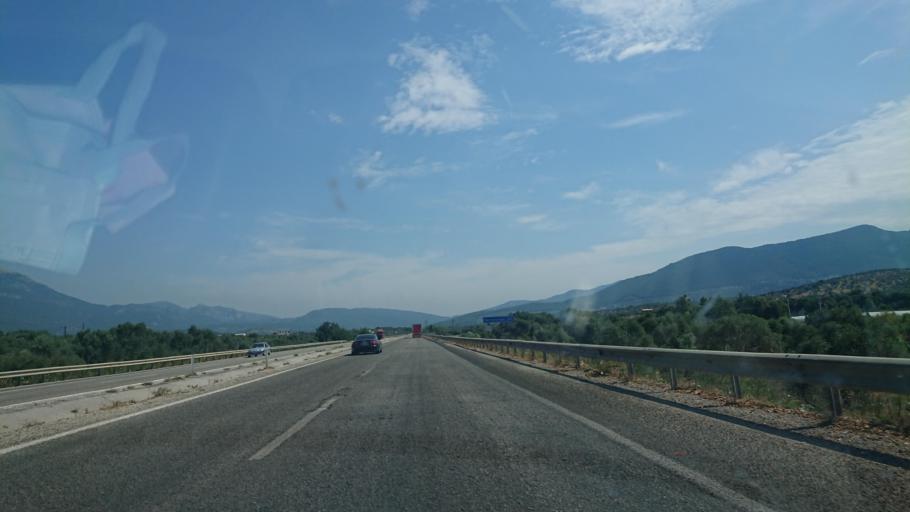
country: TR
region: Izmir
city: Dagkizilca
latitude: 38.2725
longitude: 27.3963
